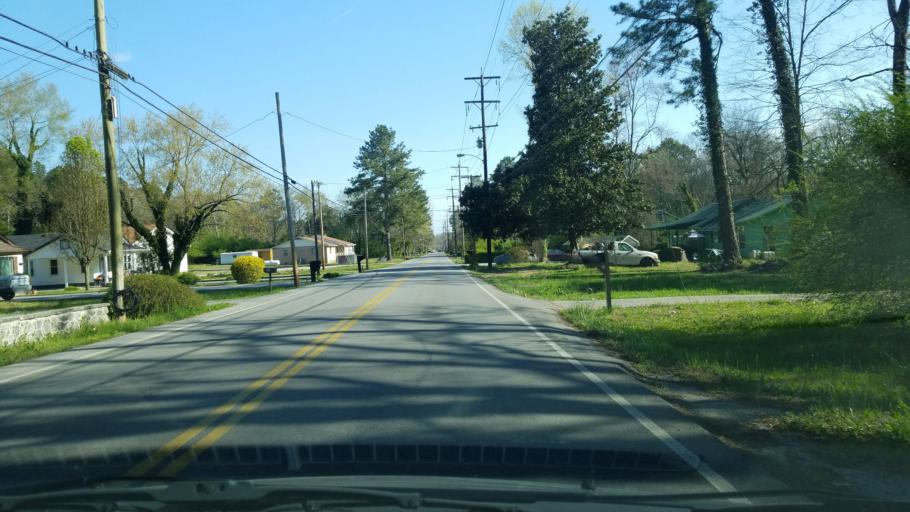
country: US
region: Tennessee
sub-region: Hamilton County
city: East Chattanooga
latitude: 35.0539
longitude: -85.2332
